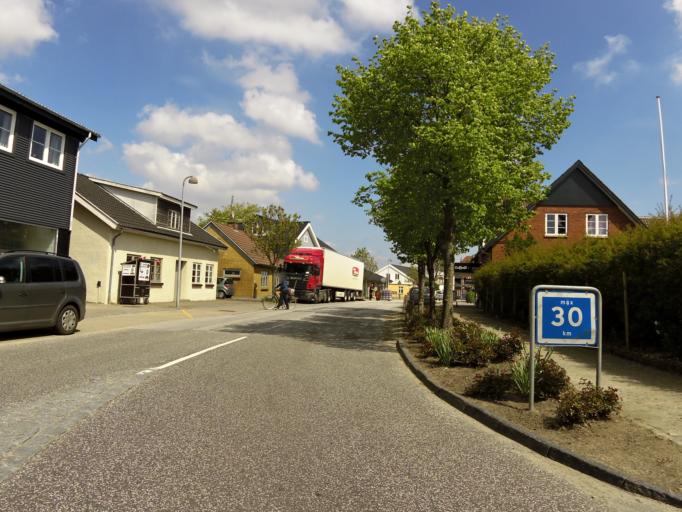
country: DK
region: South Denmark
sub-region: Tonder Kommune
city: Toftlund
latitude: 55.1929
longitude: 9.0597
